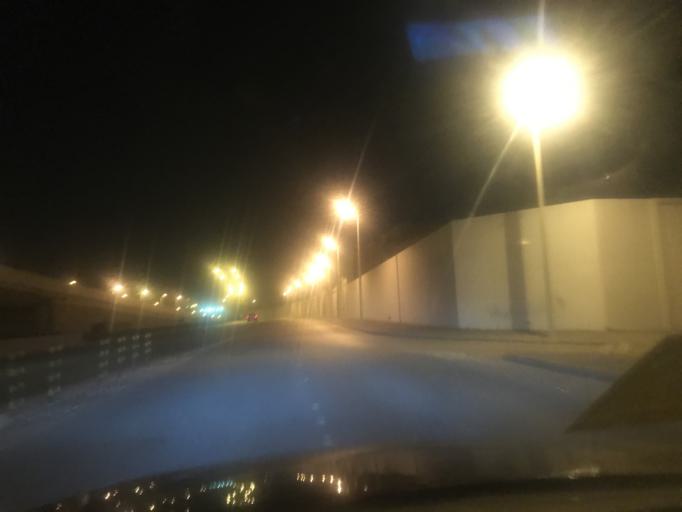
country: SA
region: Ar Riyad
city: Riyadh
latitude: 24.7021
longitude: 46.6212
